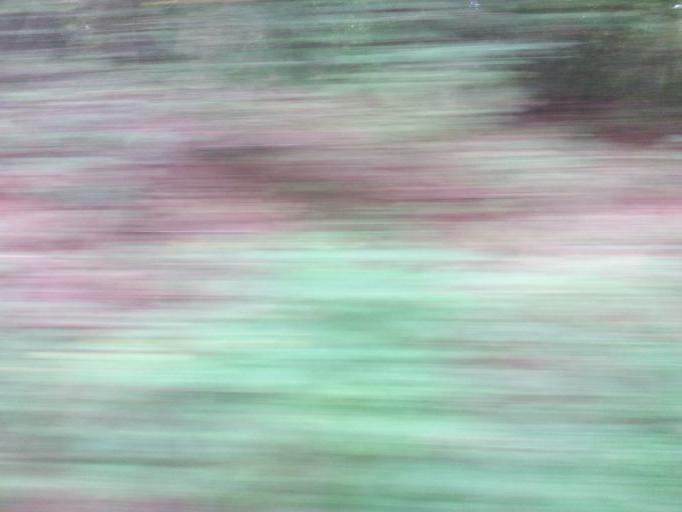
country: US
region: Tennessee
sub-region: Knox County
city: Knoxville
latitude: 35.9060
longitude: -83.8851
